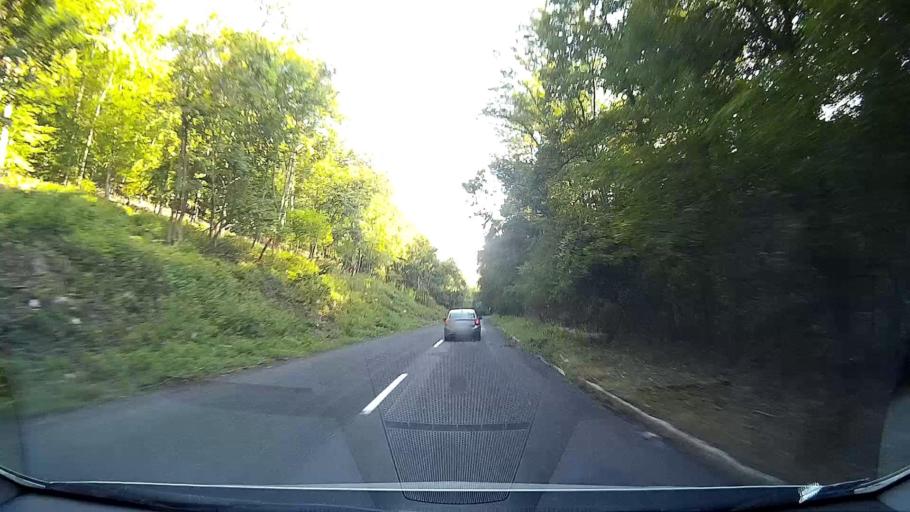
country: HU
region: Pest
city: Visegrad
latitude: 47.7496
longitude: 18.9425
